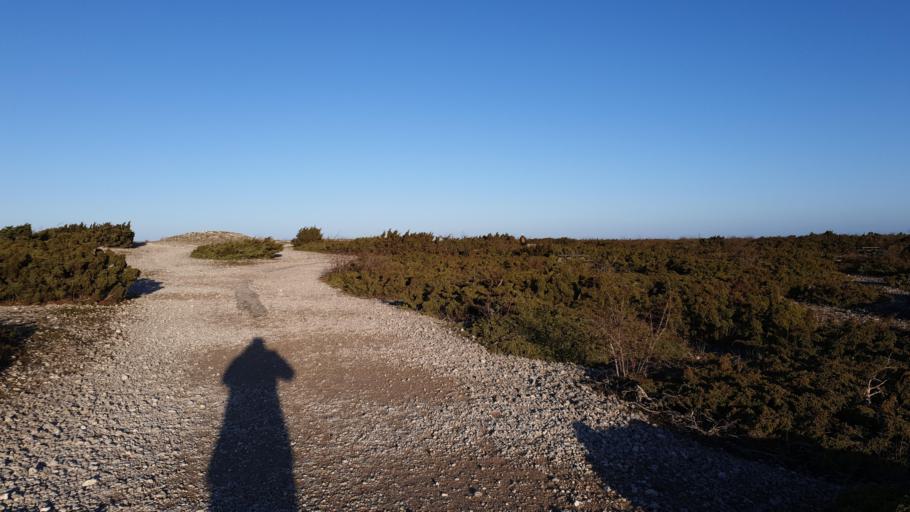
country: SE
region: Gotland
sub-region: Gotland
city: Slite
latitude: 57.9961
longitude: 19.1804
